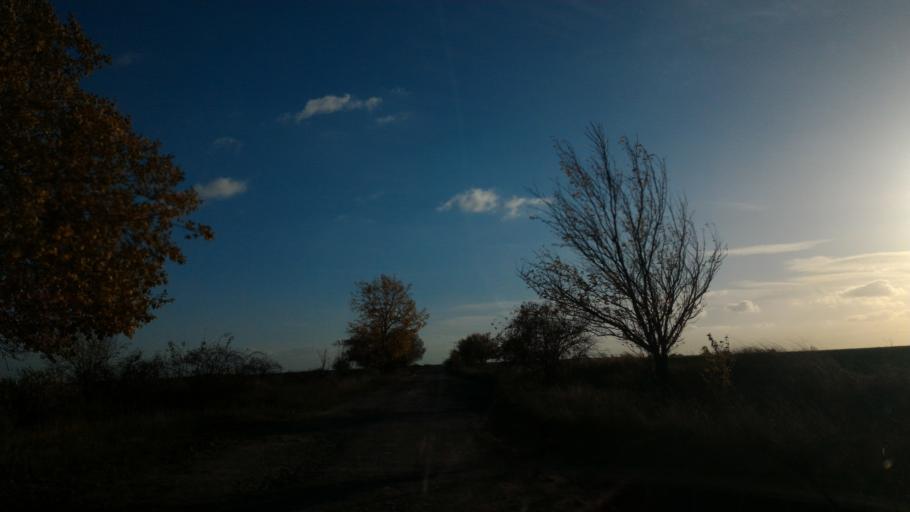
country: CZ
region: Central Bohemia
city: Bela pod Bezdezem
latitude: 50.5250
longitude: 14.7571
